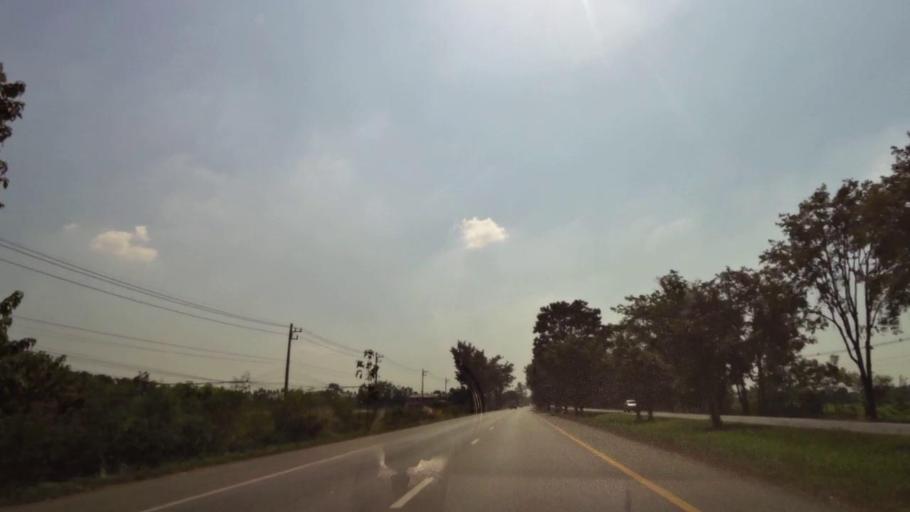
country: TH
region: Phichit
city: Bueng Na Rang
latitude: 16.1781
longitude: 100.1282
